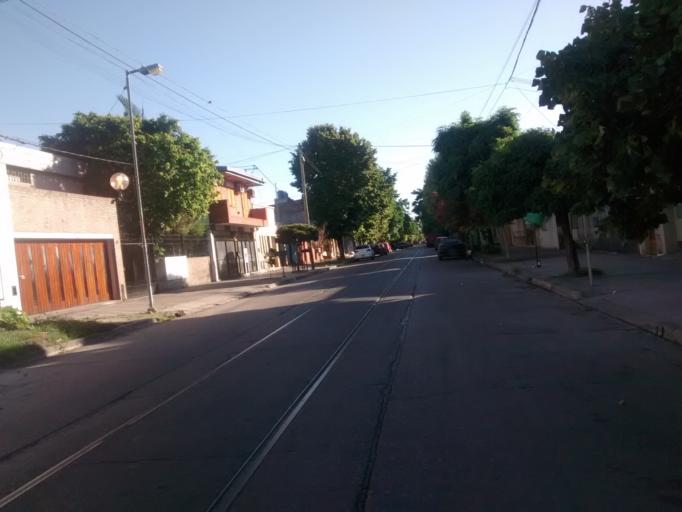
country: AR
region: Buenos Aires
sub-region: Partido de La Plata
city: La Plata
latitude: -34.9290
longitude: -57.9278
